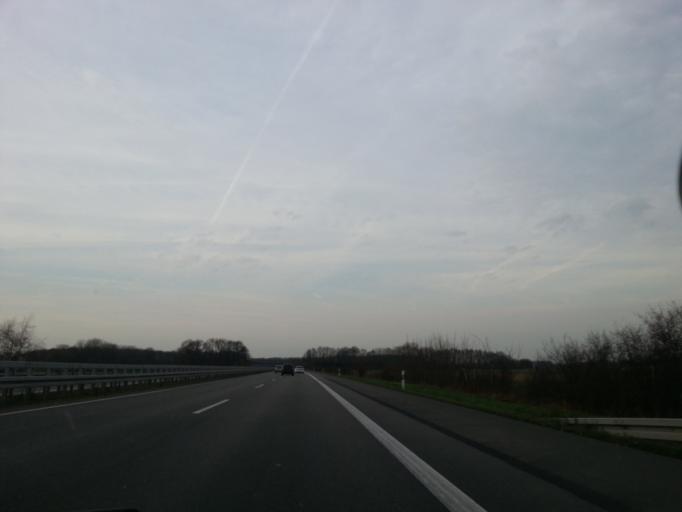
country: DE
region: North Rhine-Westphalia
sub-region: Regierungsbezirk Dusseldorf
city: Mehrhoog
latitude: 51.7708
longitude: 6.5379
